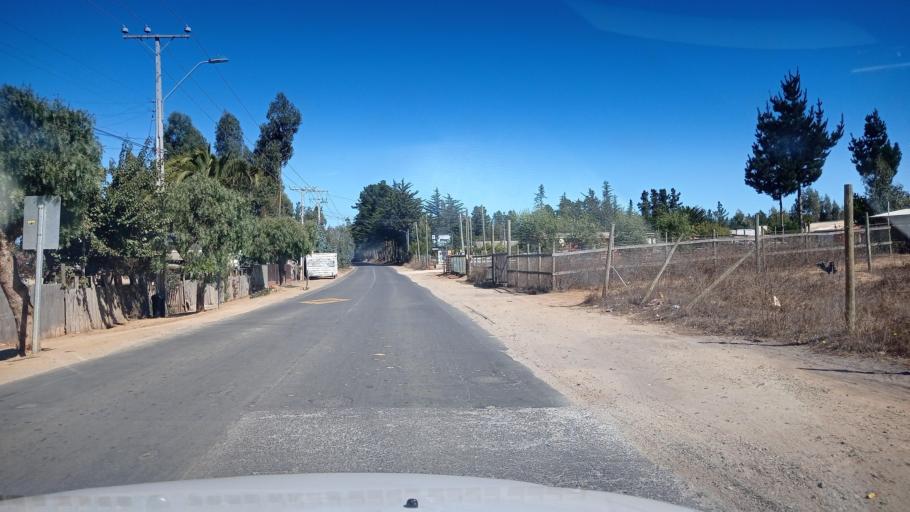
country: CL
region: O'Higgins
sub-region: Provincia de Colchagua
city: Santa Cruz
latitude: -34.4139
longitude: -71.9980
